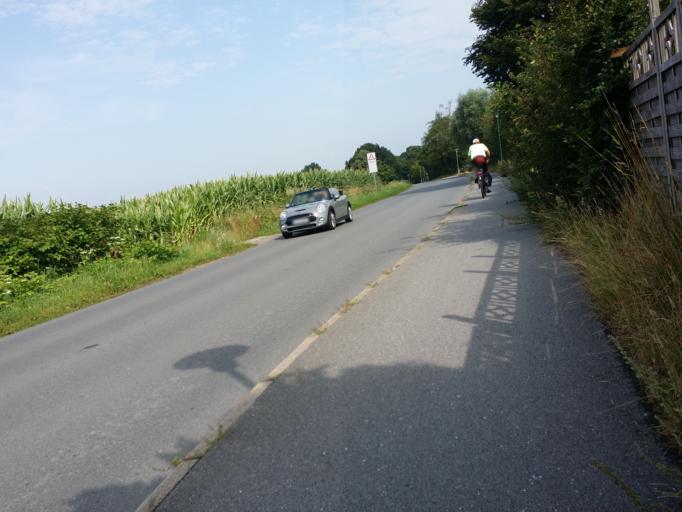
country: DE
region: Schleswig-Holstein
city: Heiligenstedten
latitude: 53.9412
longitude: 9.4694
